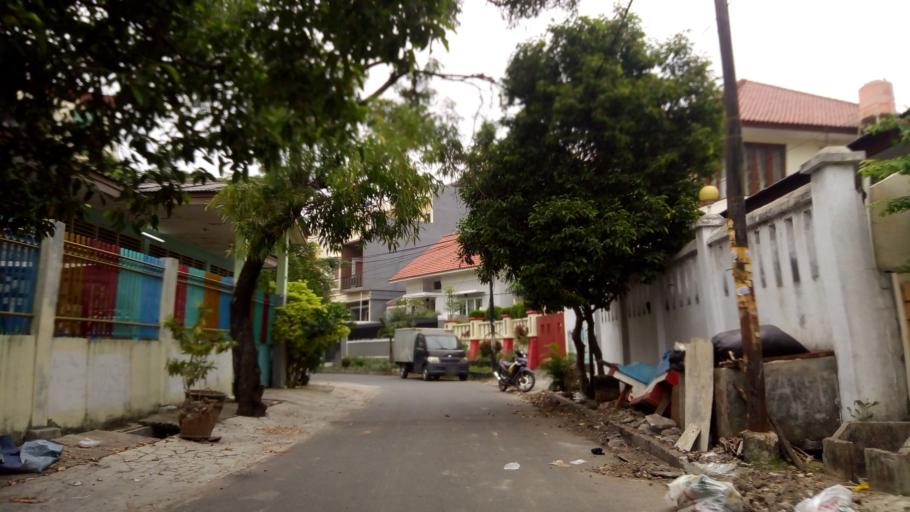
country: ID
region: Jakarta Raya
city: Jakarta
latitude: -6.1450
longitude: 106.8397
